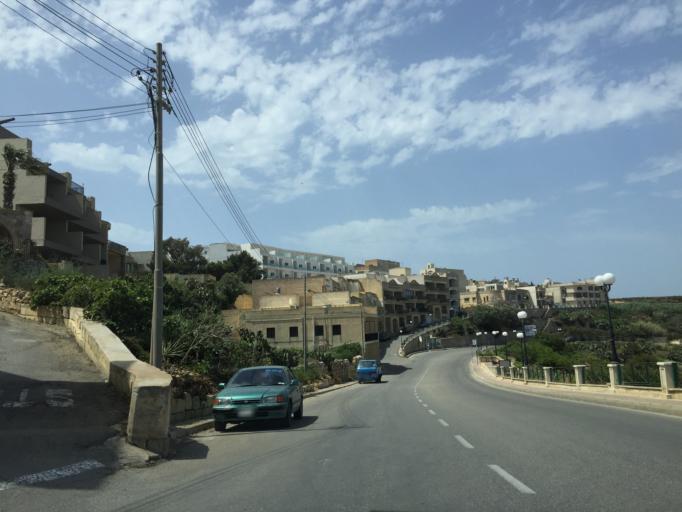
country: MT
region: In-Nadur
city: Nadur
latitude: 36.0385
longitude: 14.2869
